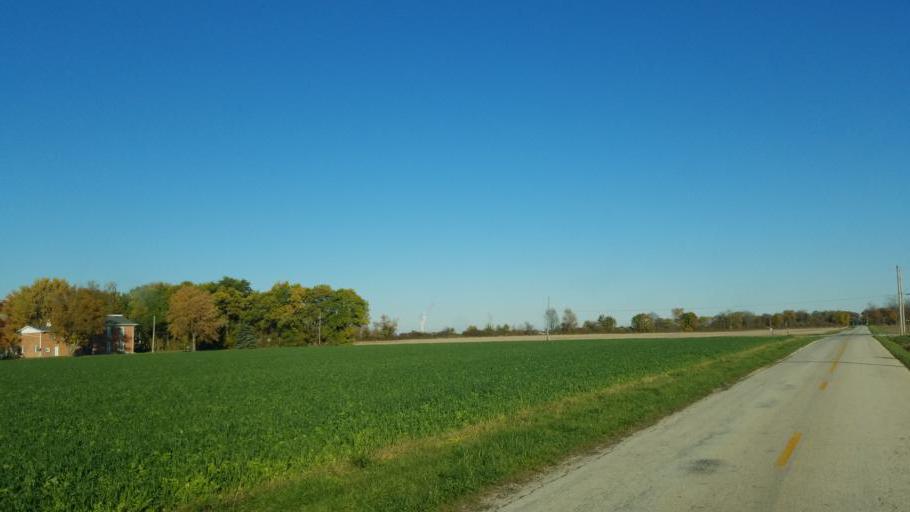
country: US
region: Ohio
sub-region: Ottawa County
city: Elmore
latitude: 41.4869
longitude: -83.3210
